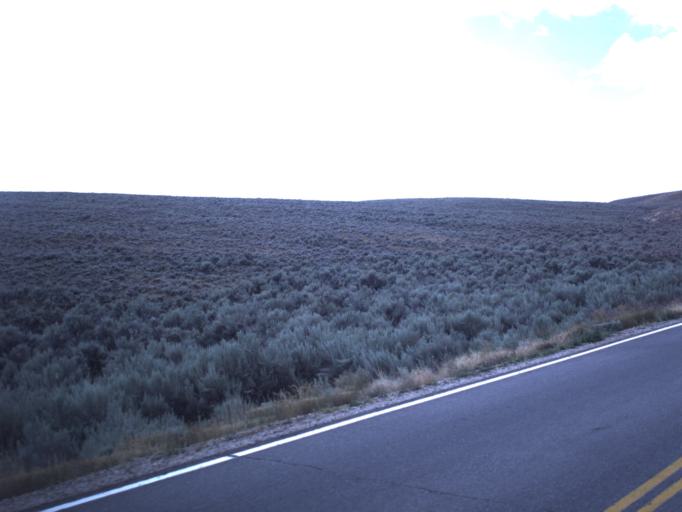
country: US
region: Utah
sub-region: Rich County
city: Randolph
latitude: 41.7778
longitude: -111.1932
